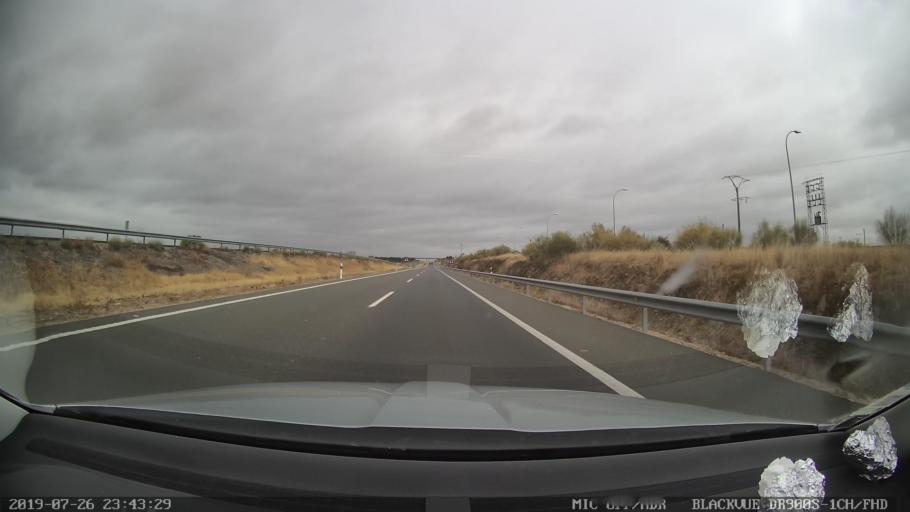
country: ES
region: Extremadura
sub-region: Provincia de Caceres
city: Trujillo
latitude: 39.5270
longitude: -5.8340
